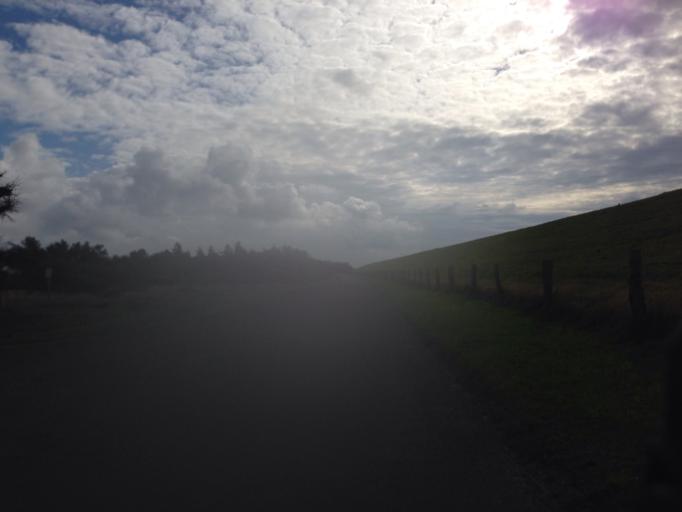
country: DE
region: Schleswig-Holstein
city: Utersum
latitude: 54.7263
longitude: 8.4034
